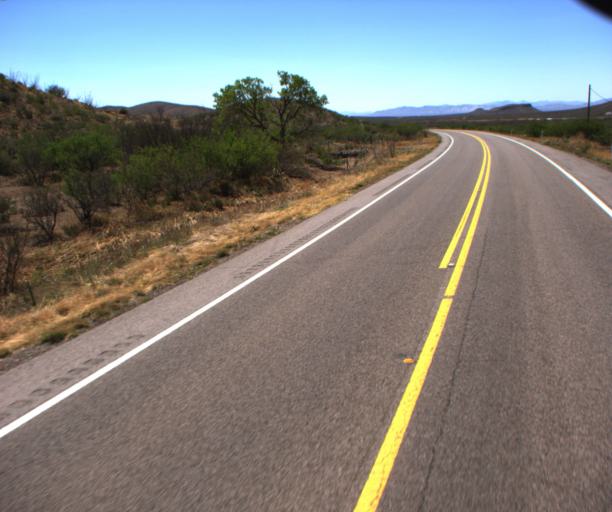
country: US
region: Arizona
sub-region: Cochise County
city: Douglas
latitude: 31.4784
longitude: -109.4471
